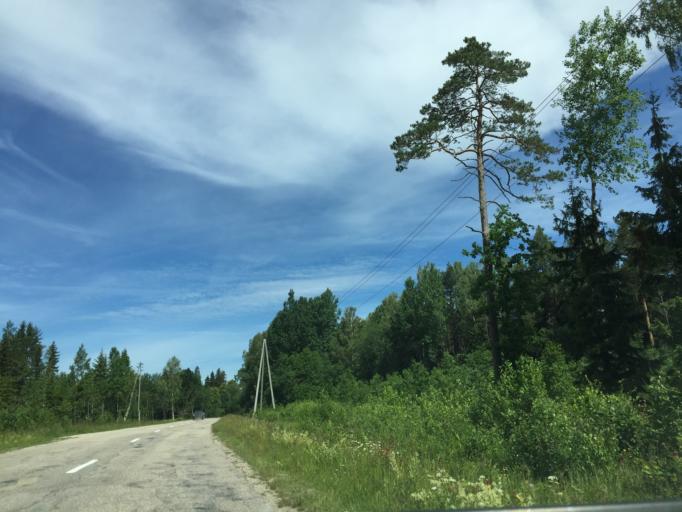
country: LV
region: Dundaga
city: Dundaga
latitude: 57.5678
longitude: 22.3079
